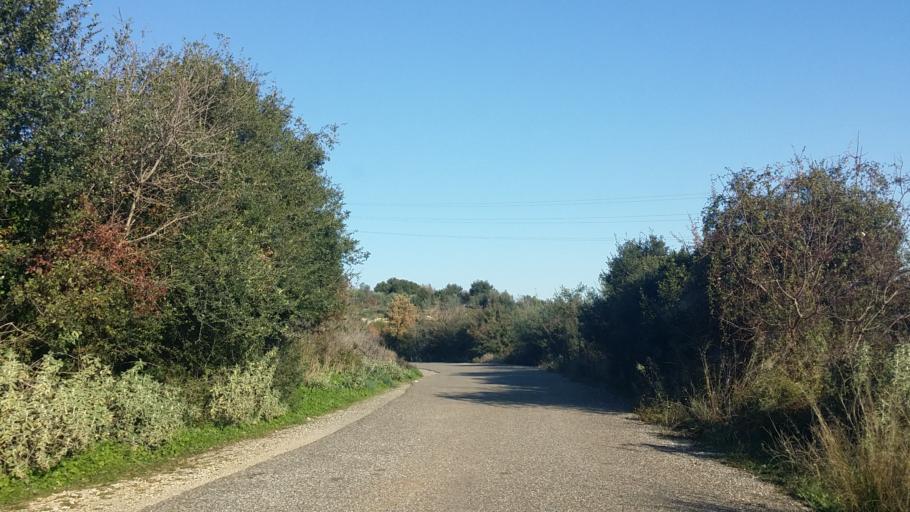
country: GR
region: West Greece
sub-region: Nomos Aitolias kai Akarnanias
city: Katouna
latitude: 38.7538
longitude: 21.1442
